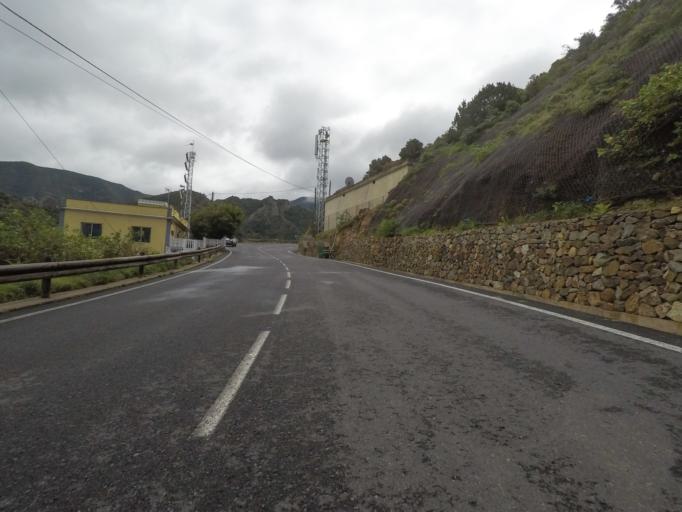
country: ES
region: Canary Islands
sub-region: Provincia de Santa Cruz de Tenerife
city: Vallehermosa
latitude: 28.1675
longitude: -17.2773
